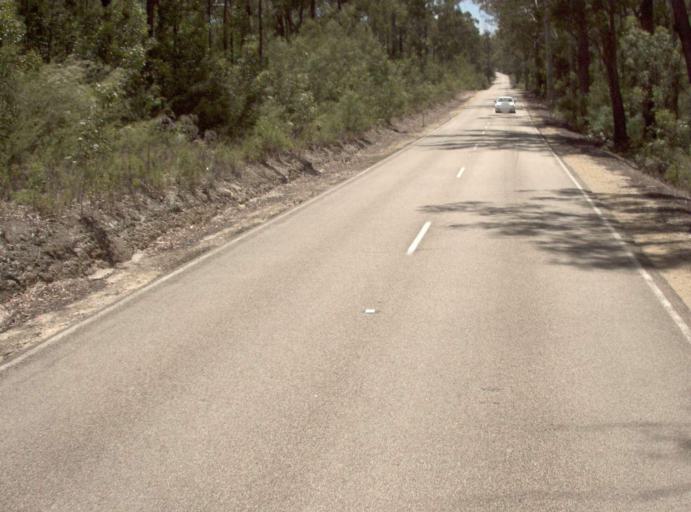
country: AU
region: Victoria
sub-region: East Gippsland
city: Lakes Entrance
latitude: -37.6473
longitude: 147.8937
